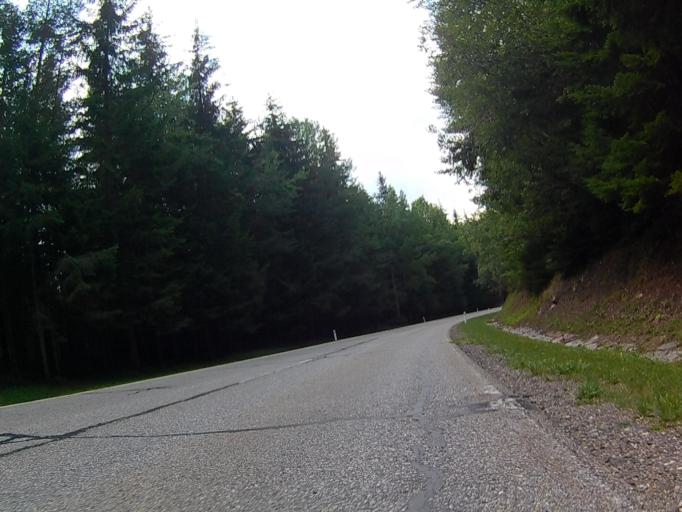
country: AT
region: Styria
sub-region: Politischer Bezirk Deutschlandsberg
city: Soboth
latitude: 46.6835
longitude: 15.0897
